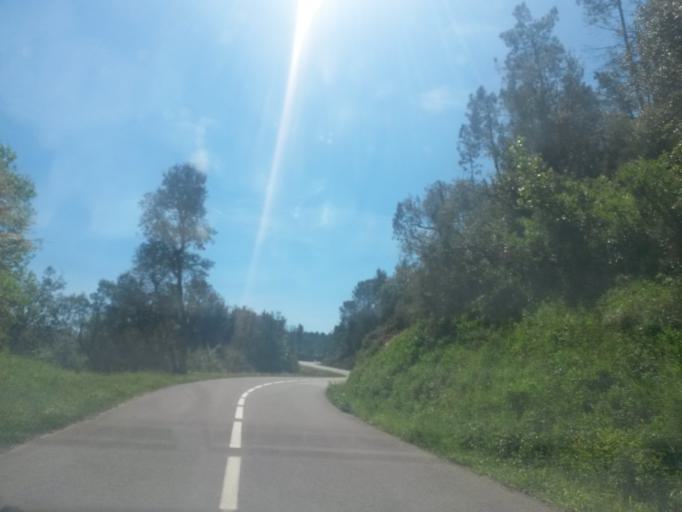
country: ES
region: Catalonia
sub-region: Provincia de Girona
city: Madremanya
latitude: 41.9385
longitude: 2.9489
